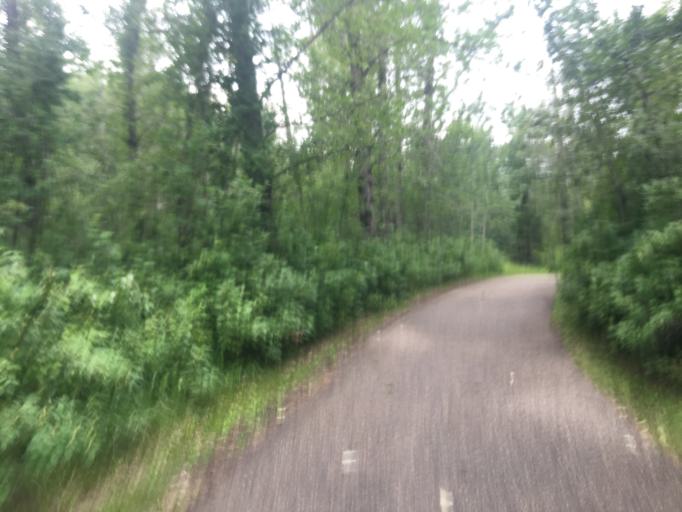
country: CA
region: Alberta
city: Grande Prairie
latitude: 55.1541
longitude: -118.8033
